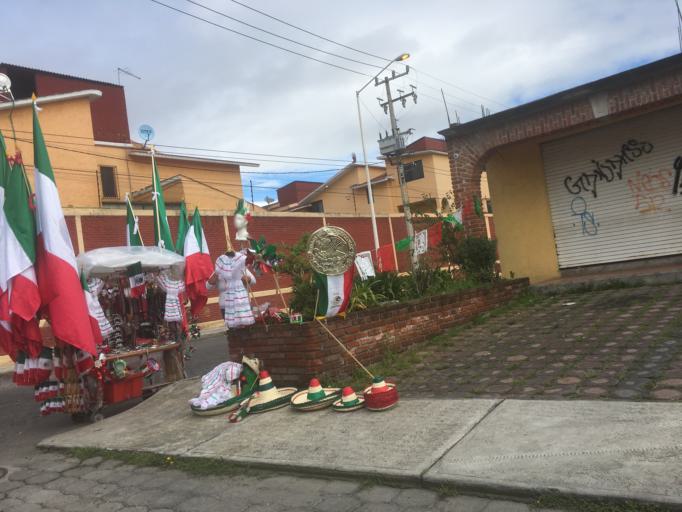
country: MX
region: Morelos
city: Metepec
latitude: 19.2591
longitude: -99.6093
